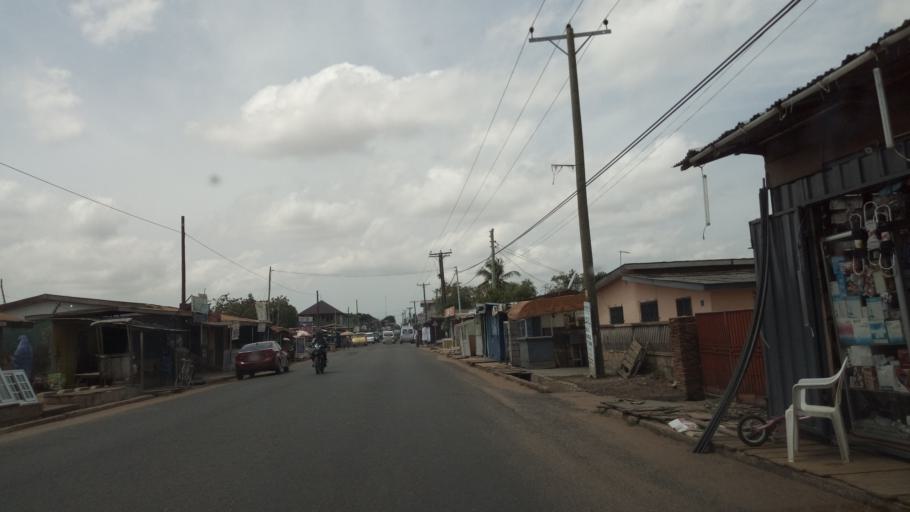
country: GH
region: Greater Accra
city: Medina Estates
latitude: 5.6817
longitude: -0.1605
